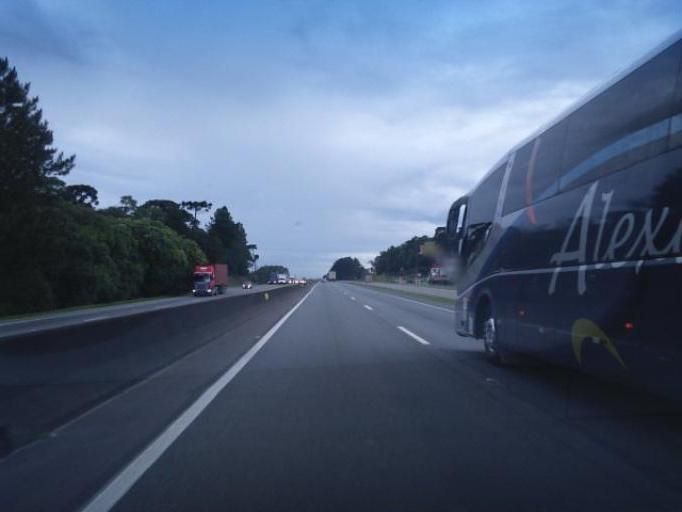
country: BR
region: Parana
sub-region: Sao Jose Dos Pinhais
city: Sao Jose dos Pinhais
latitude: -25.6511
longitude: -49.1575
